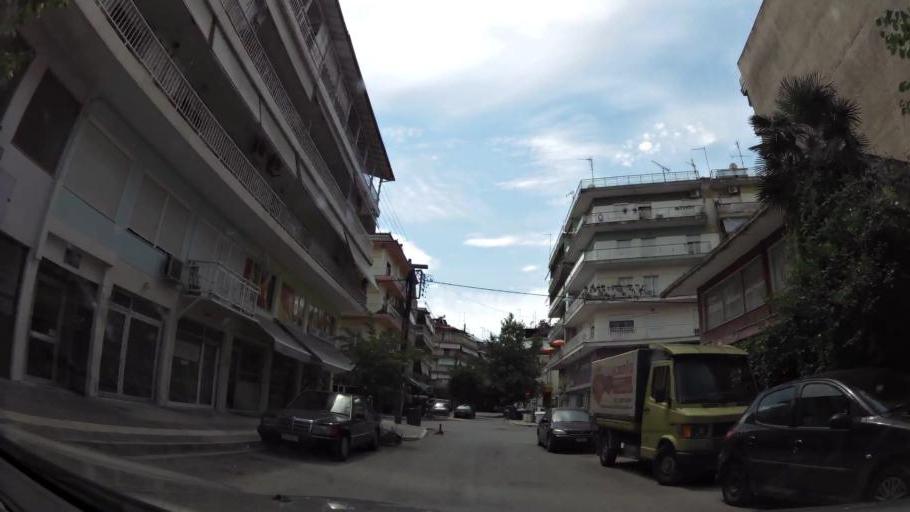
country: GR
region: Central Macedonia
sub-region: Nomos Pierias
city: Katerini
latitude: 40.2740
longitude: 22.5108
